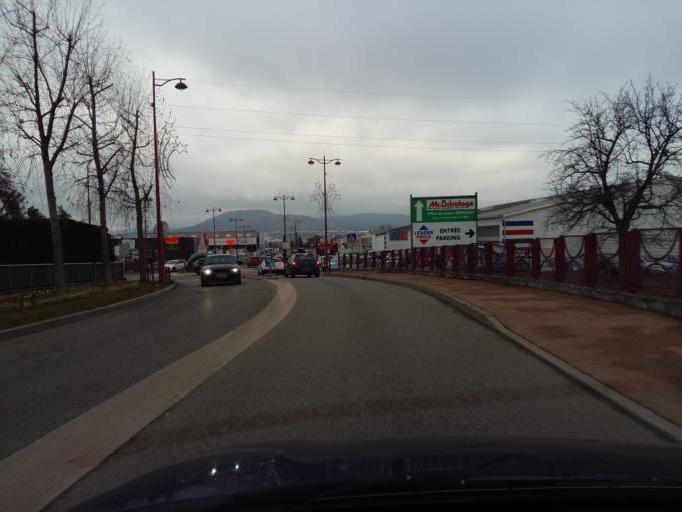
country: FR
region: Rhone-Alpes
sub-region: Departement de l'Ardeche
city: Davezieux
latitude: 45.2557
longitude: 4.7021
